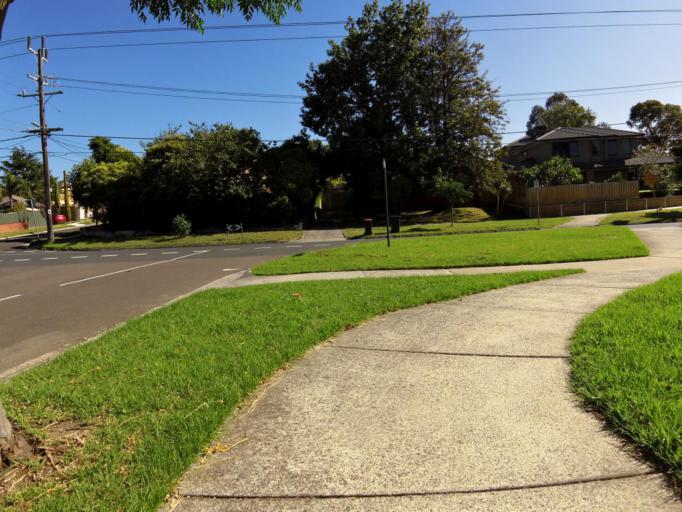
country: AU
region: Victoria
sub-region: Monash
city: Ashwood
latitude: -37.8741
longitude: 145.1002
